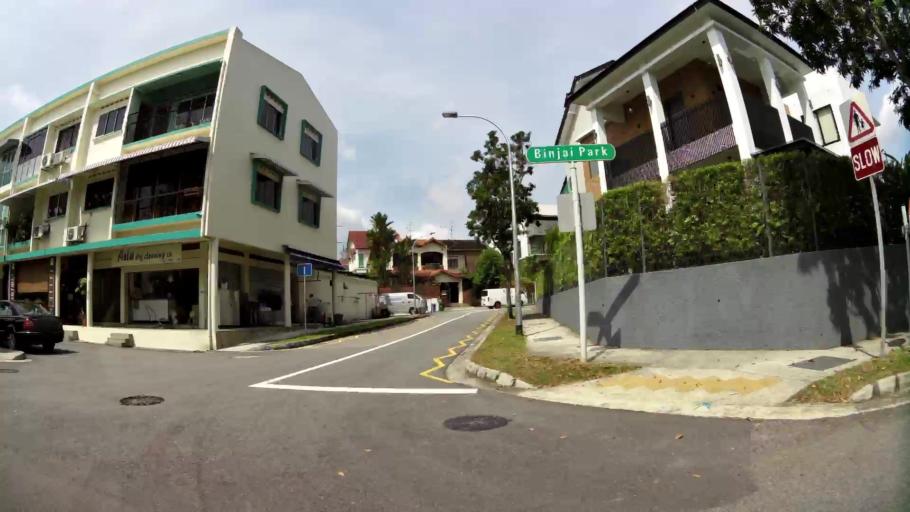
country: SG
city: Singapore
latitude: 1.3368
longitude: 103.7872
